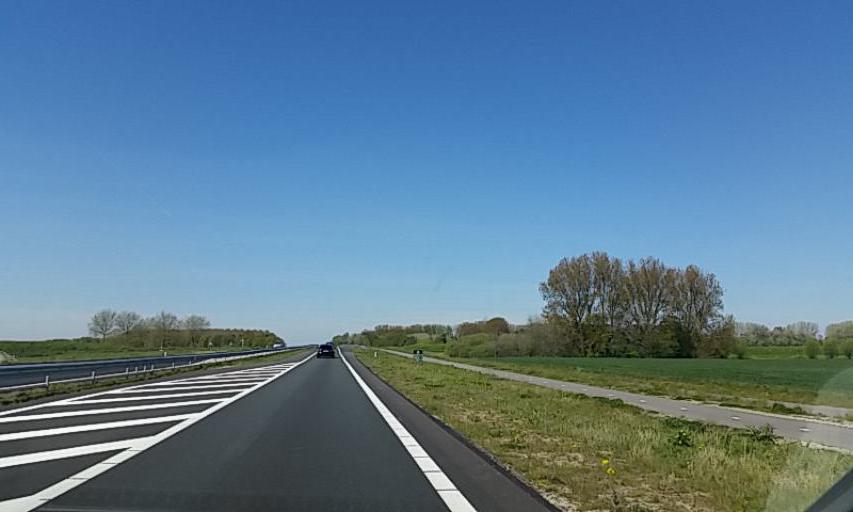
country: BE
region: Flanders
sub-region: Provincie Oost-Vlaanderen
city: Assenede
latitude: 51.3124
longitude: 3.7396
